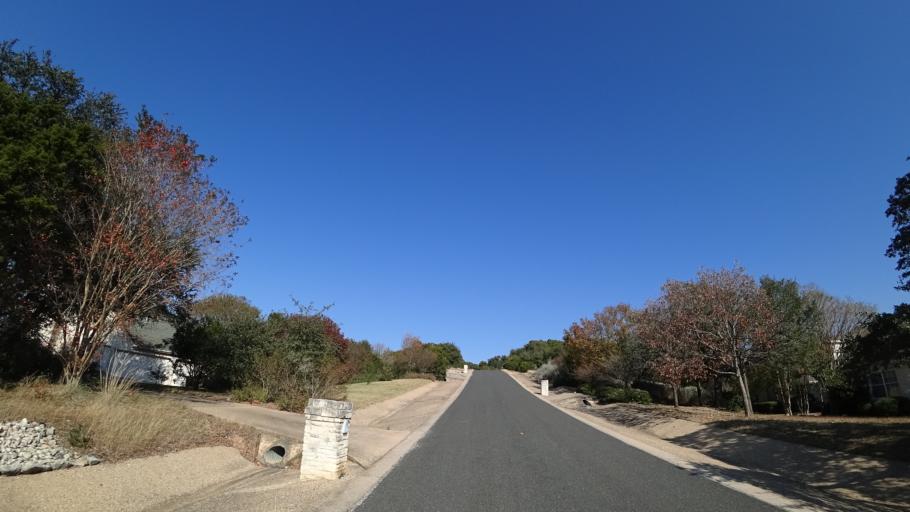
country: US
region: Texas
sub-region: Travis County
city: West Lake Hills
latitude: 30.3752
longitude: -97.8251
